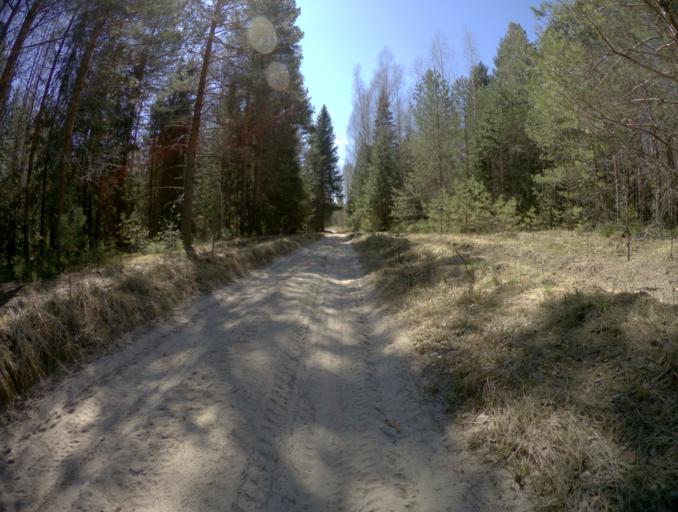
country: RU
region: Vladimir
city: Golovino
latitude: 55.8859
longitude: 40.4070
